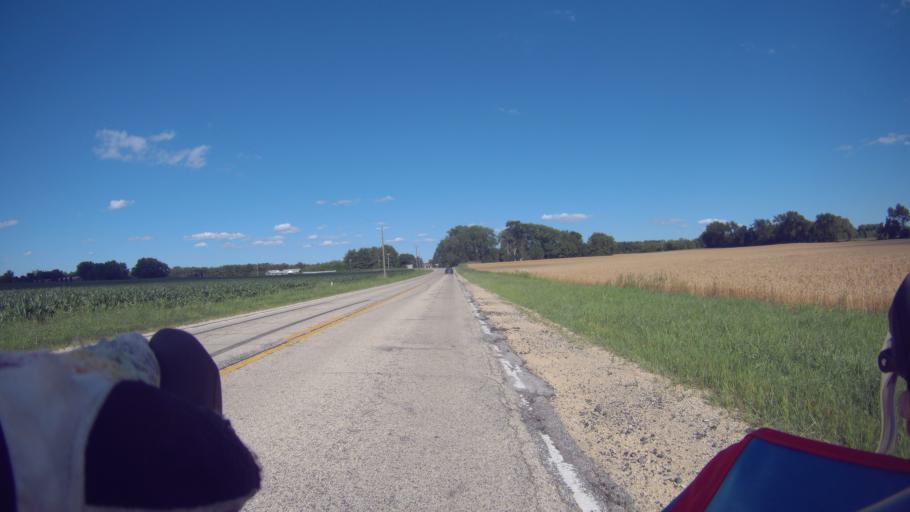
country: US
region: Wisconsin
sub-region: Dane County
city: Stoughton
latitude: 42.8928
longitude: -89.2591
